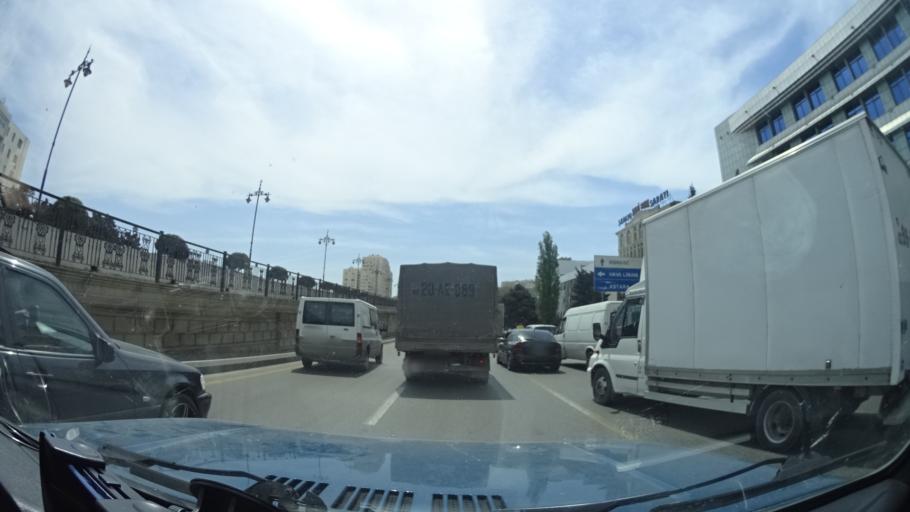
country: AZ
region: Baki
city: Khodzhi-Gasan
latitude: 40.4057
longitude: 49.8064
